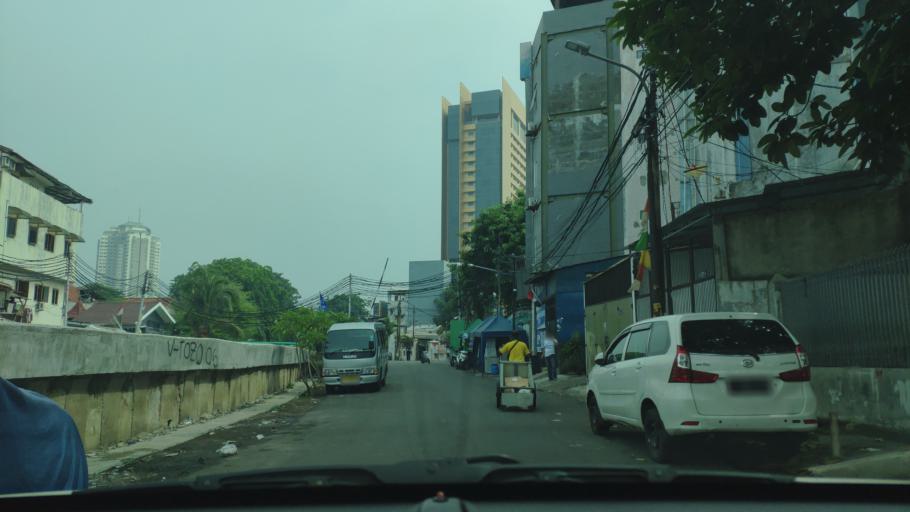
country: ID
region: Jakarta Raya
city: Jakarta
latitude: -6.1639
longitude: 106.8147
